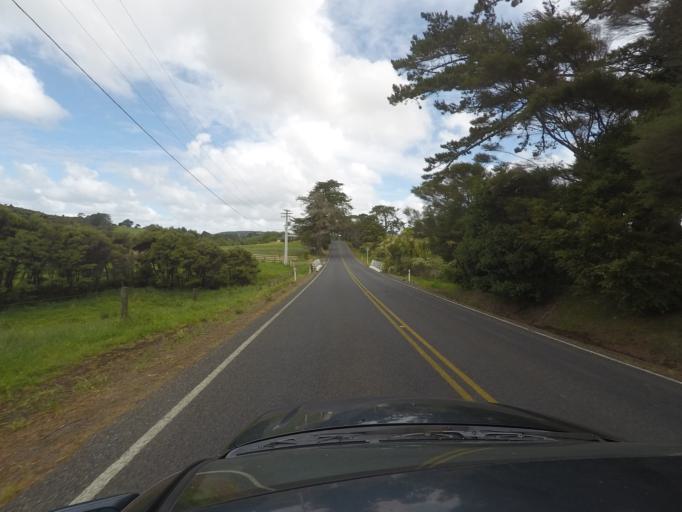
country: NZ
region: Auckland
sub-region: Auckland
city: Parakai
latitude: -36.6493
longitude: 174.5201
